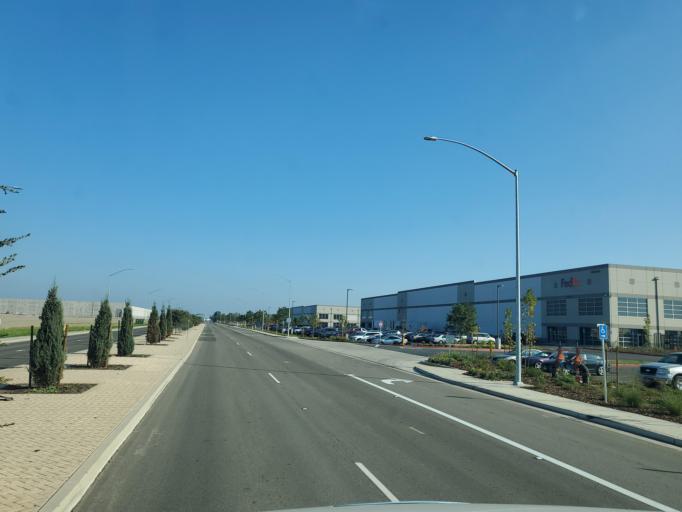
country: US
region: California
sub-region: San Joaquin County
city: Kennedy
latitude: 37.9053
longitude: -121.1990
